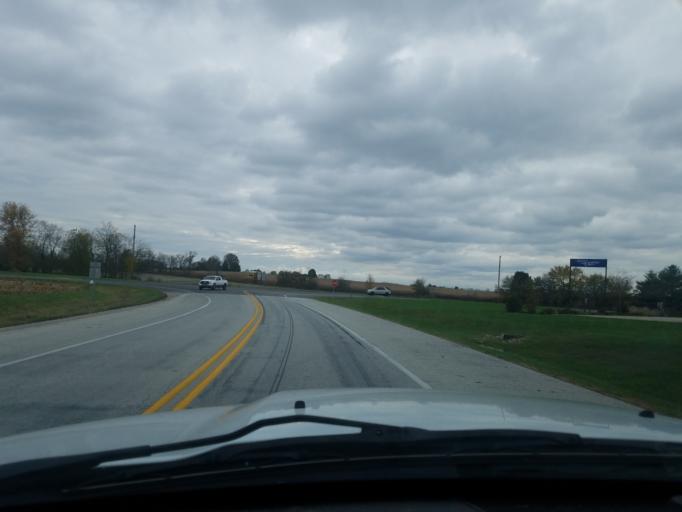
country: US
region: Indiana
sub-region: Bartholomew County
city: Columbus
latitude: 39.1723
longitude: -85.8497
